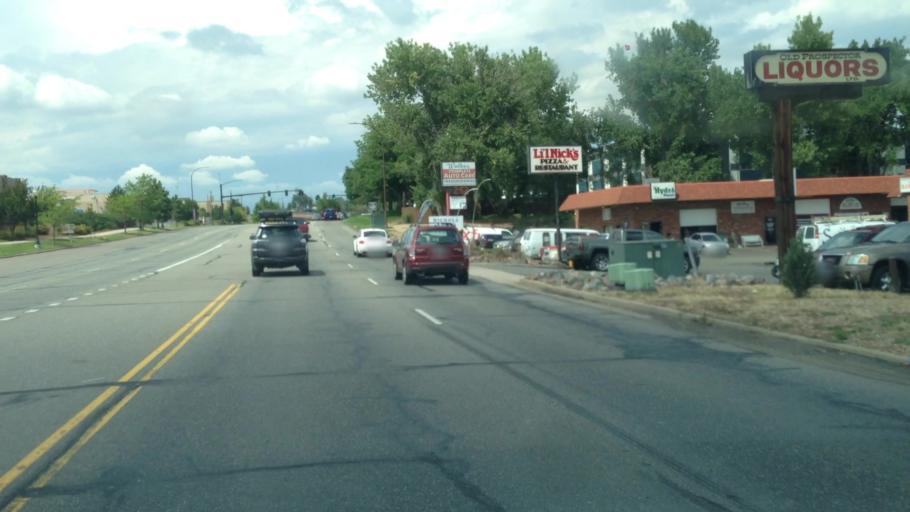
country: US
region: Colorado
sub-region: Jefferson County
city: Arvada
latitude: 39.7881
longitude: -105.1095
